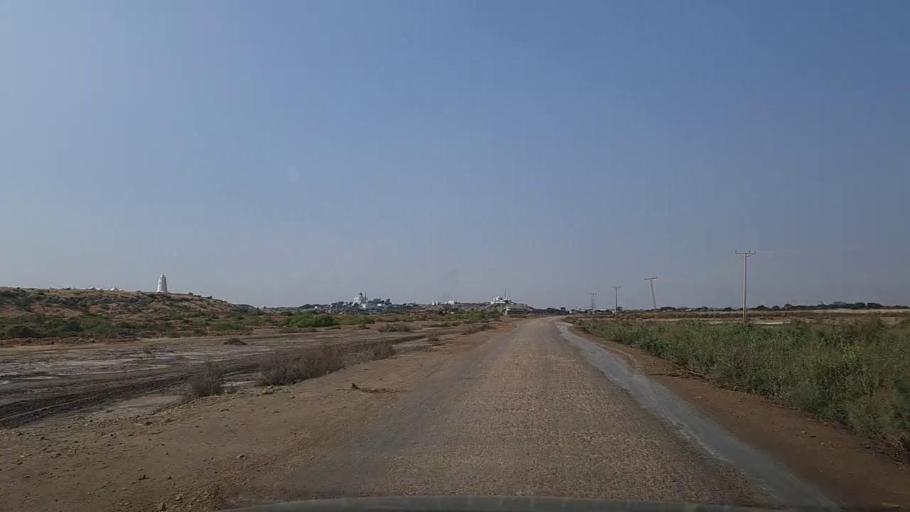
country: PK
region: Sindh
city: Chuhar Jamali
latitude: 24.5541
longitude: 67.8896
